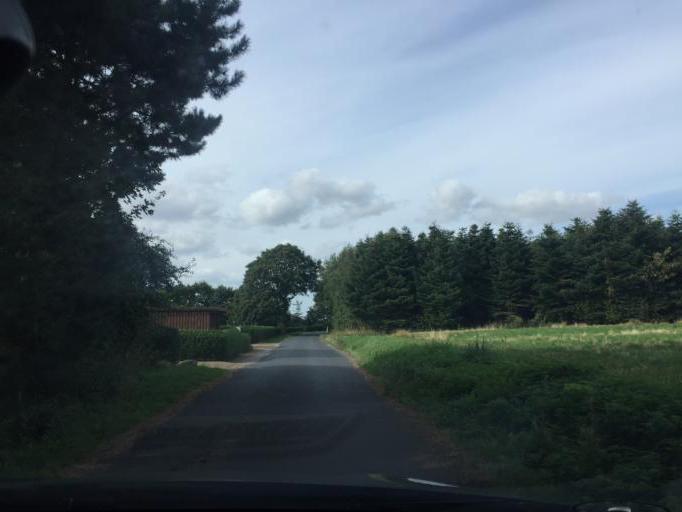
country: DK
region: South Denmark
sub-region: Faaborg-Midtfyn Kommune
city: Arslev
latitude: 55.3426
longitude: 10.5124
